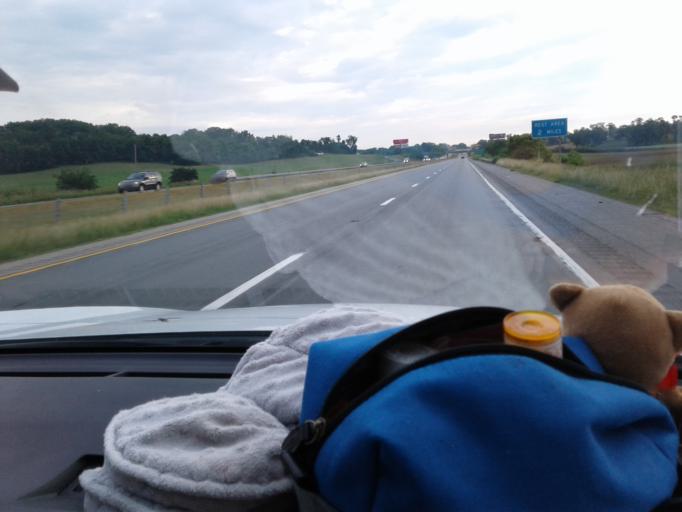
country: US
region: Pennsylvania
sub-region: Cumberland County
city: Newville
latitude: 40.1124
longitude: -77.3765
